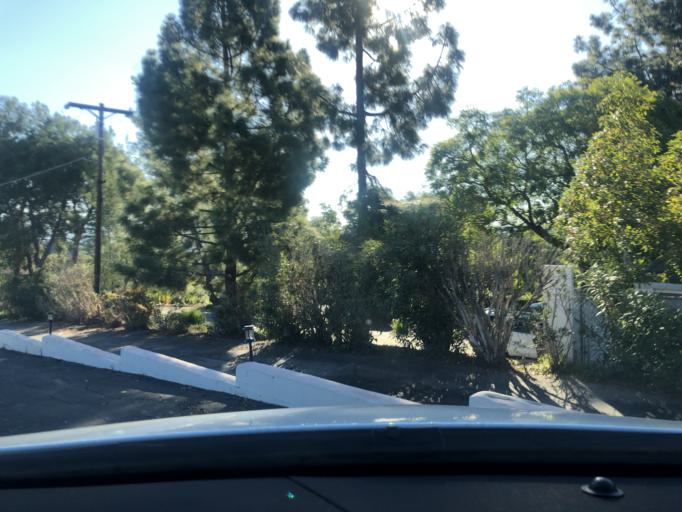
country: US
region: California
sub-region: San Diego County
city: Casa de Oro-Mount Helix
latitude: 32.7682
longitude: -116.9618
